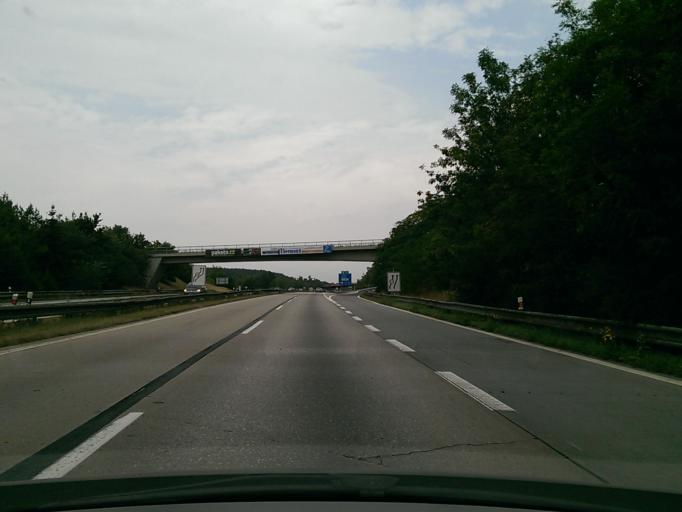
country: CZ
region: South Moravian
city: Troubsko
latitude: 49.1877
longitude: 16.4519
